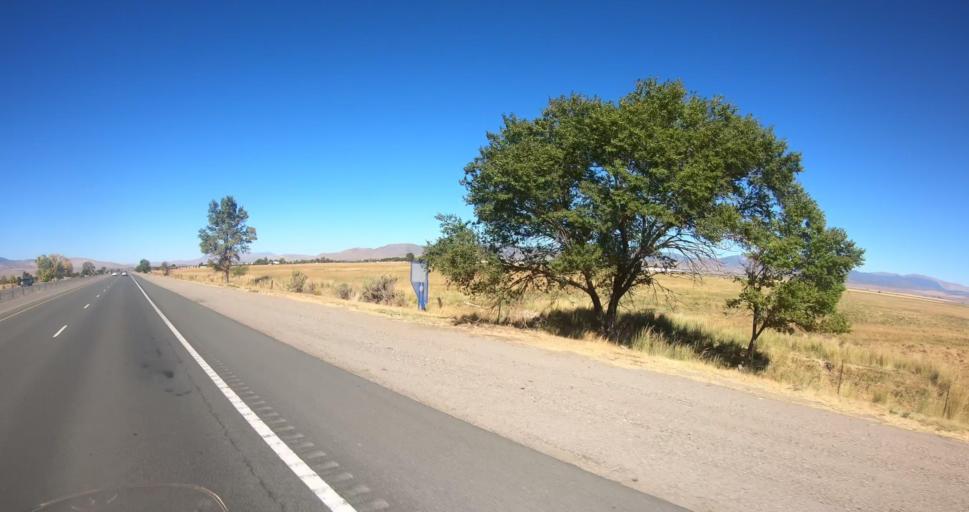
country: US
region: Nevada
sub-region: Douglas County
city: Minden
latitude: 38.9876
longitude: -119.7777
